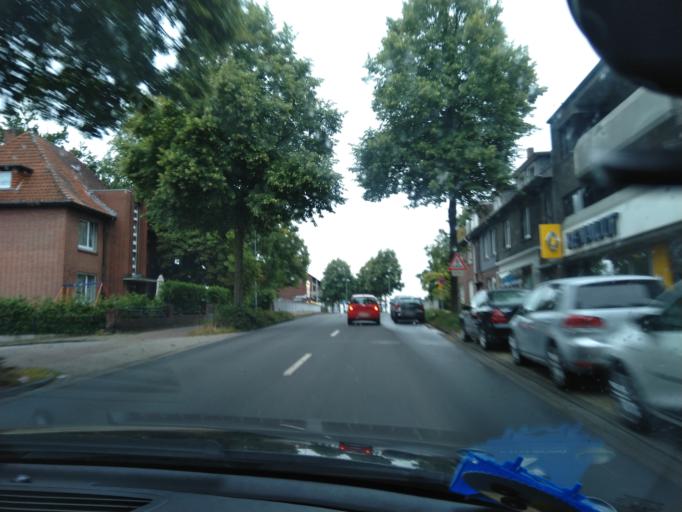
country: DE
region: Lower Saxony
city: Nordhorn
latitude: 52.4263
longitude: 7.0756
